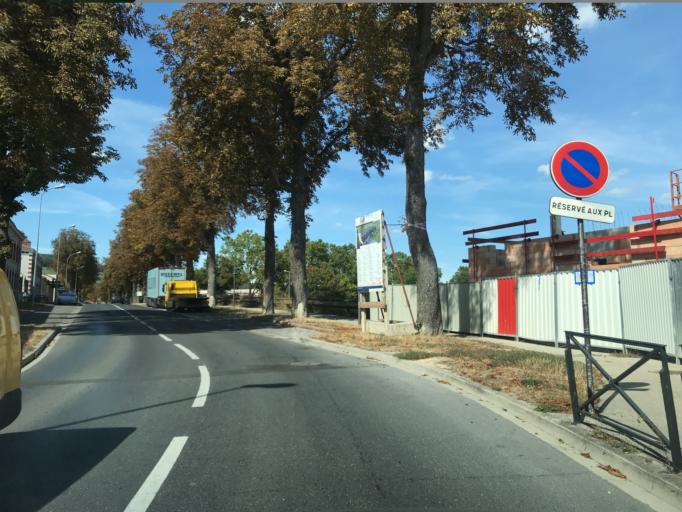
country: FR
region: Champagne-Ardenne
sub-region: Departement de la Marne
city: Pierry
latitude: 49.0280
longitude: 3.9572
